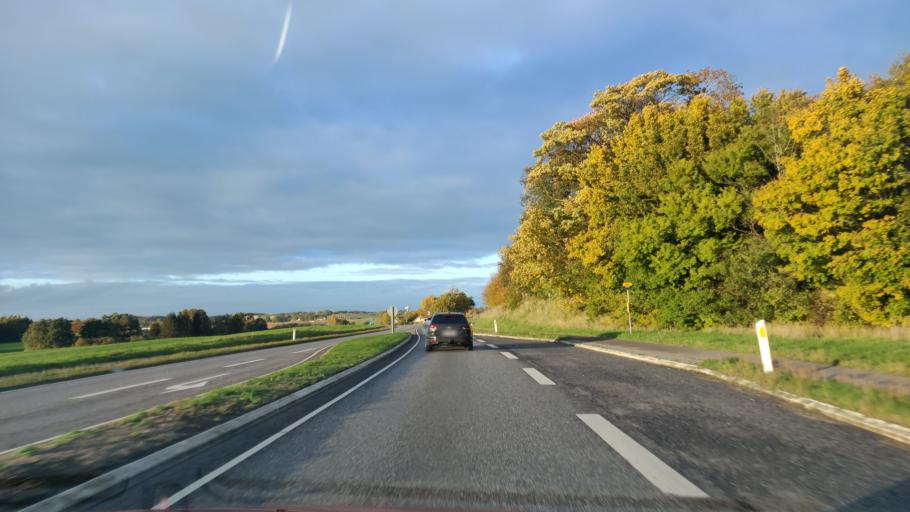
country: DK
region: Zealand
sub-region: Holbaek Kommune
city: Holbaek
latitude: 55.6751
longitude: 11.6911
